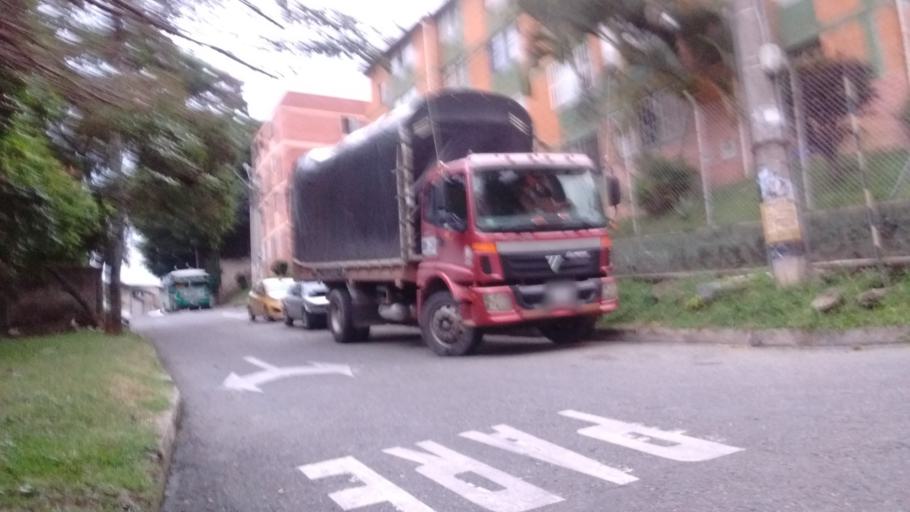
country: CO
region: Antioquia
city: Medellin
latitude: 6.2813
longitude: -75.5882
